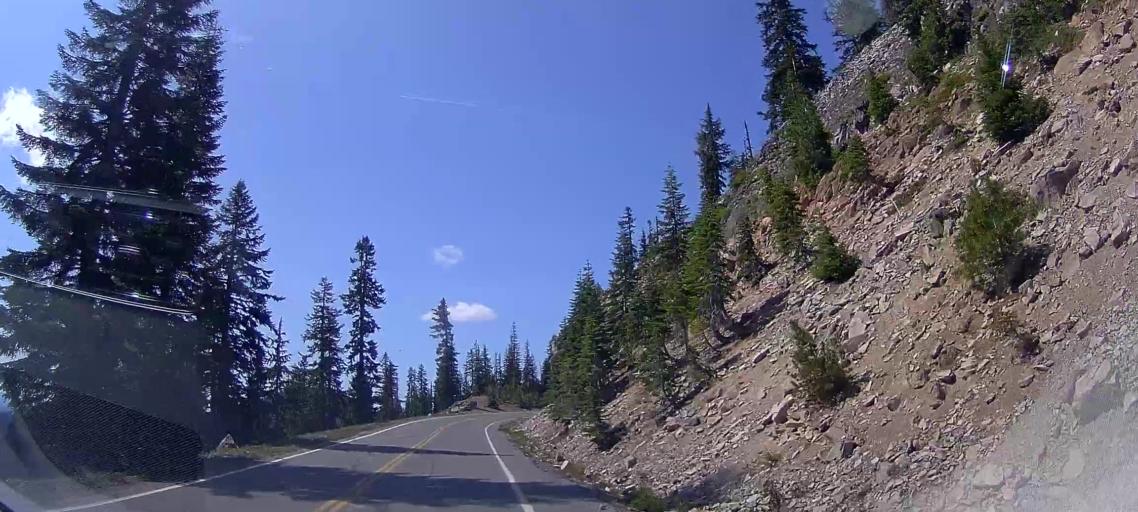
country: US
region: Oregon
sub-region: Klamath County
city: Klamath Falls
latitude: 42.8776
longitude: -122.1039
